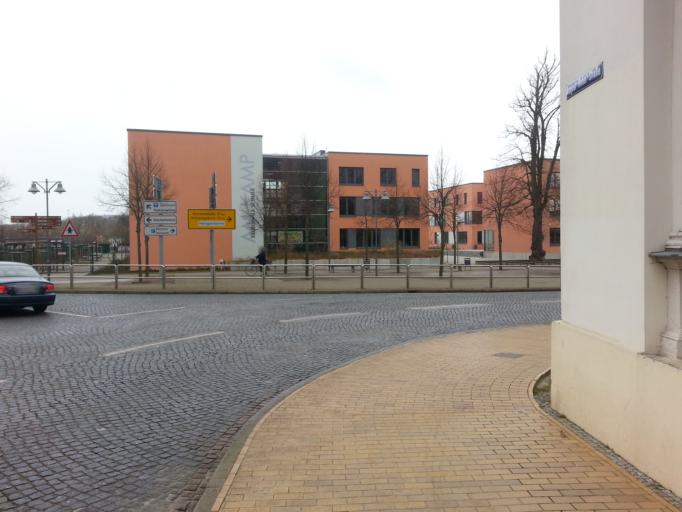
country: DE
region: Mecklenburg-Vorpommern
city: Bad Doberan
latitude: 54.1066
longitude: 11.9038
